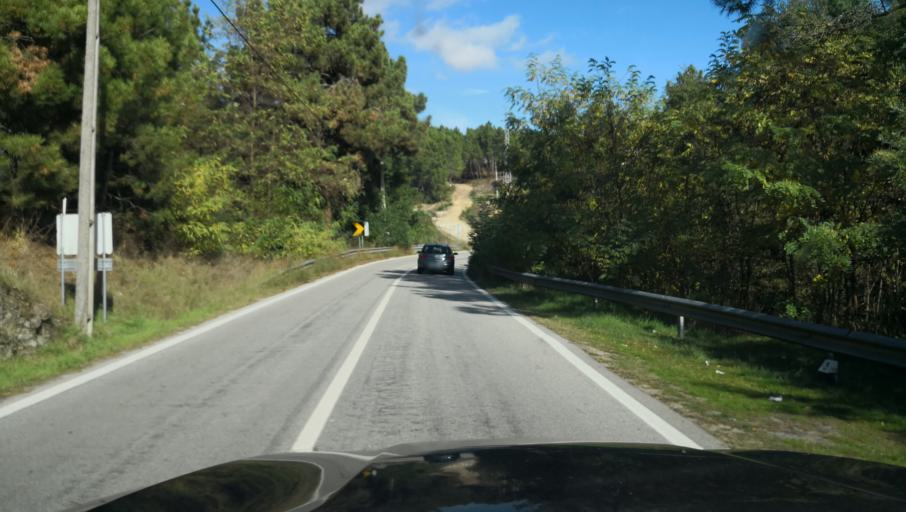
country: PT
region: Vila Real
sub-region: Chaves
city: Chaves
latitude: 41.7201
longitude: -7.4978
